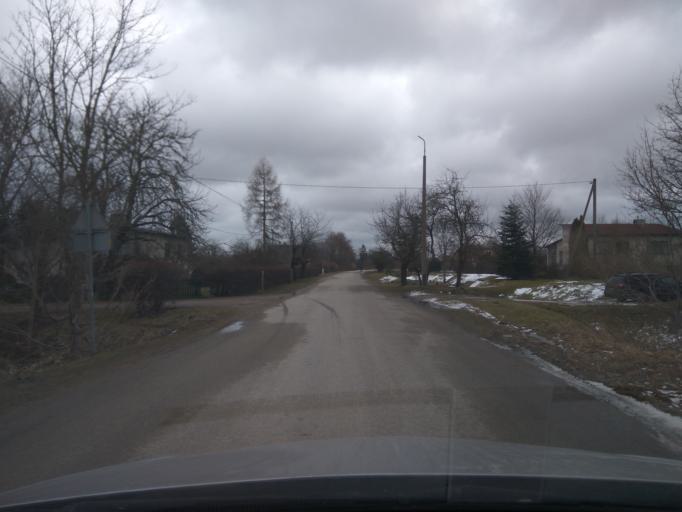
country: LV
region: Ventspils
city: Ventspils
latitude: 57.3324
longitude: 21.6484
